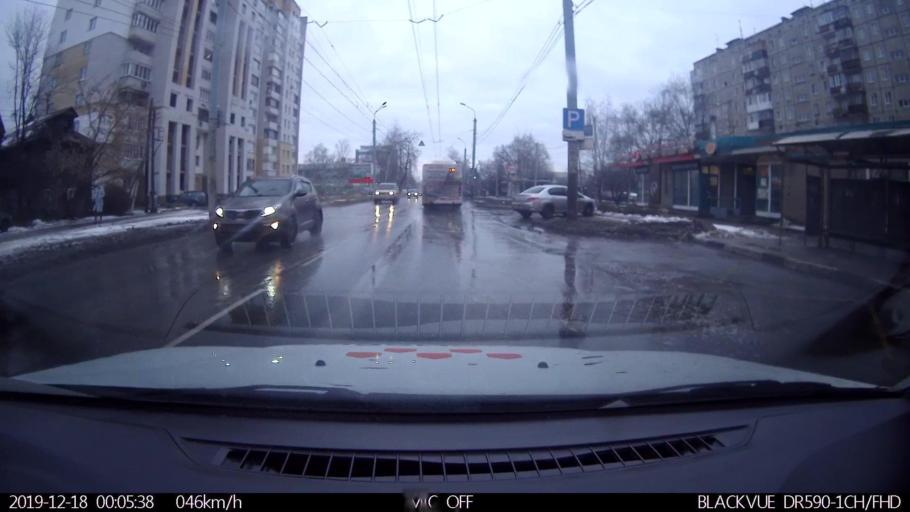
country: RU
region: Nizjnij Novgorod
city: Neklyudovo
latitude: 56.3625
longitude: 43.8581
